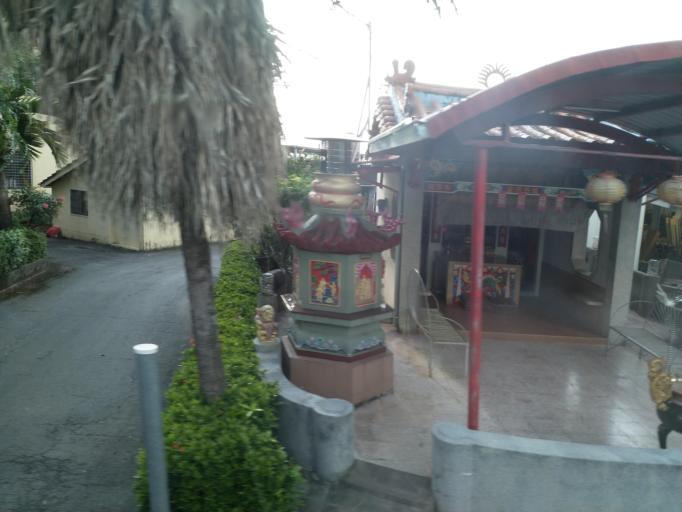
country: TW
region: Taiwan
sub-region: Pingtung
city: Pingtung
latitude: 22.8770
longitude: 120.5357
